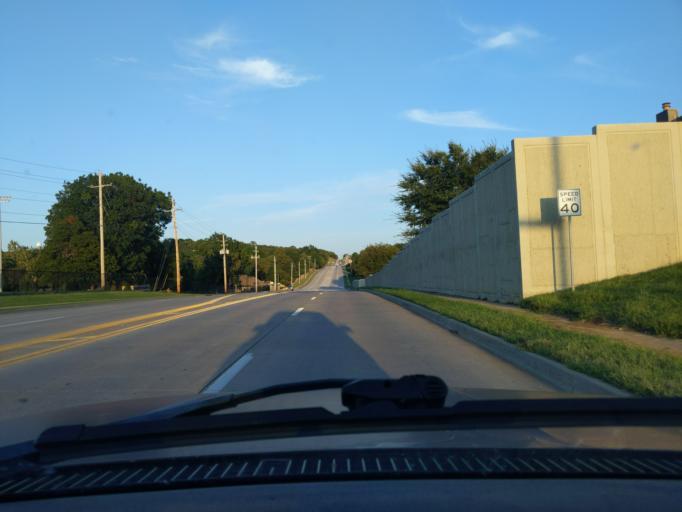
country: US
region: Oklahoma
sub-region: Tulsa County
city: Jenks
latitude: 36.0463
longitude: -95.9486
